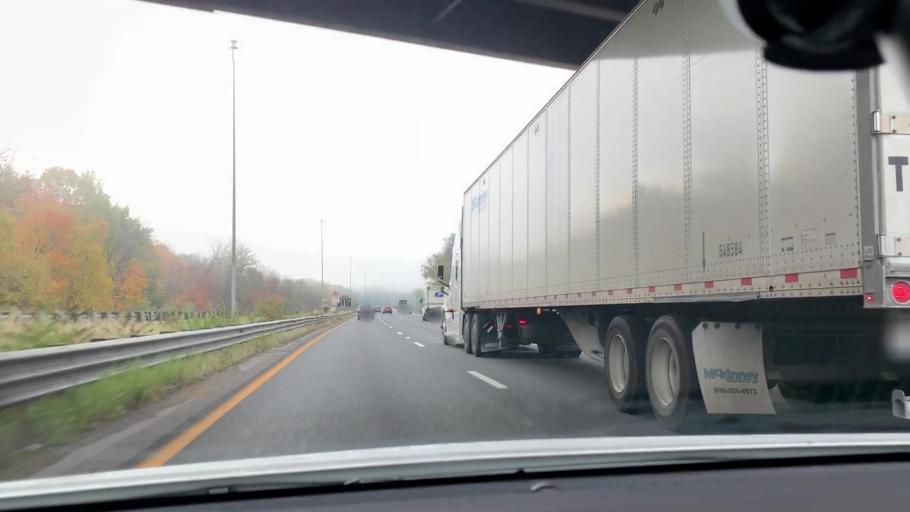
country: US
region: Massachusetts
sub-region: Hampden County
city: Longmeadow
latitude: 42.0365
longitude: -72.5889
